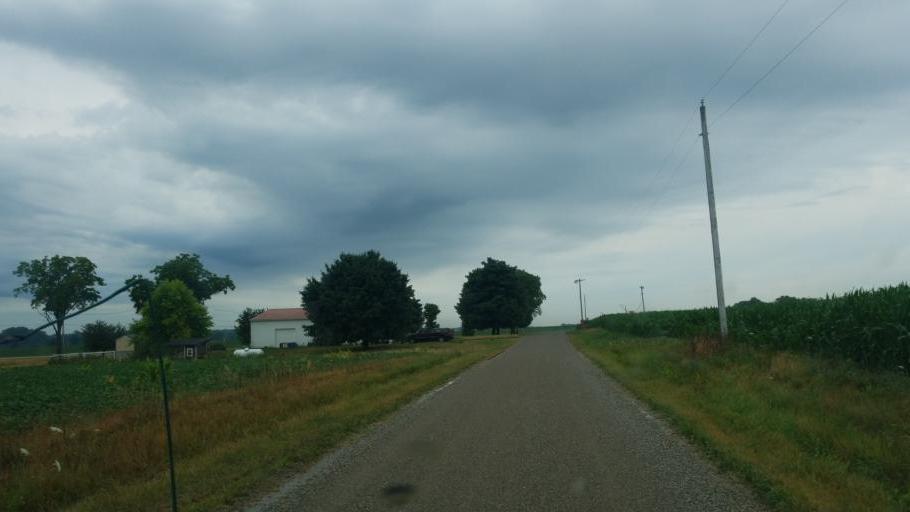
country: US
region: Indiana
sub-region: Steuben County
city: Hamilton
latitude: 41.4969
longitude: -84.9414
